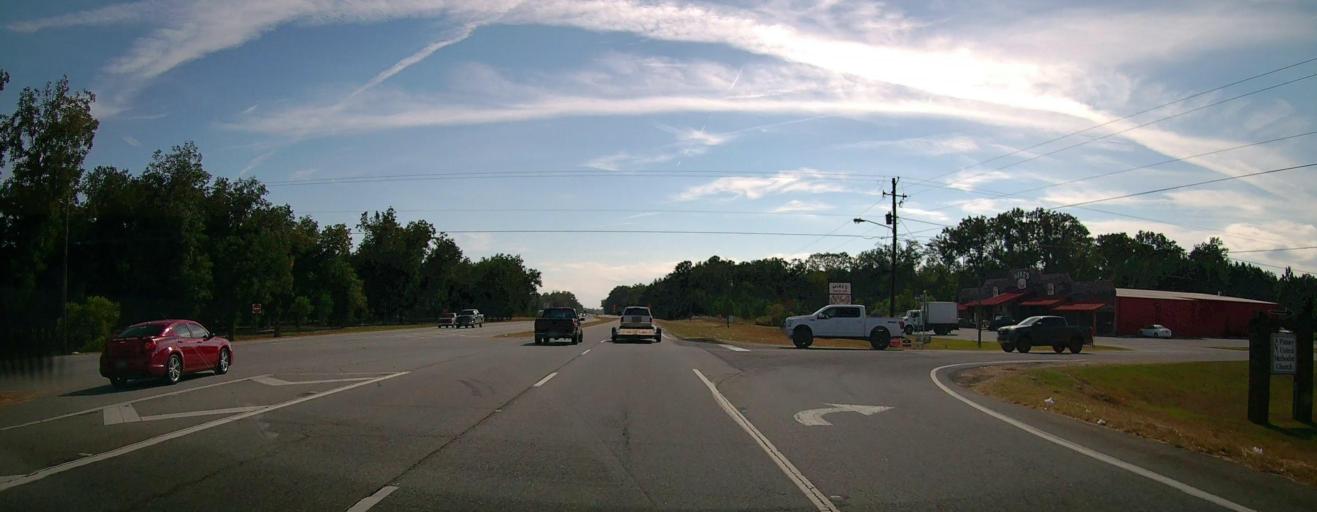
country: US
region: Georgia
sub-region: Dougherty County
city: Putney
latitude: 31.4708
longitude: -84.1179
